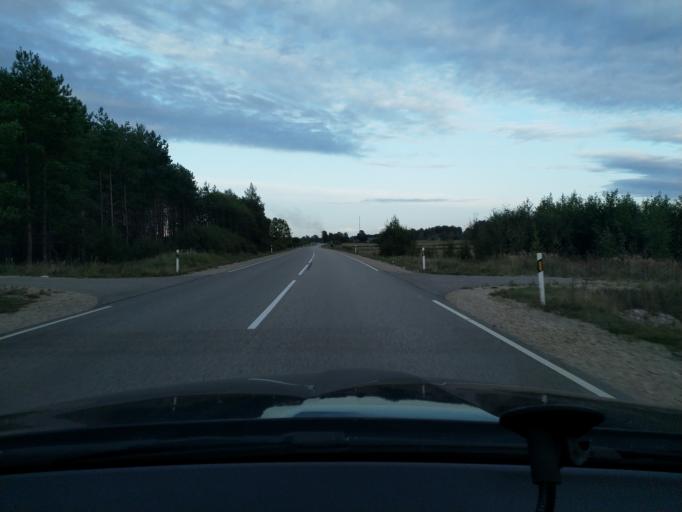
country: LV
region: Kandava
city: Kandava
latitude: 56.9250
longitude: 22.7756
